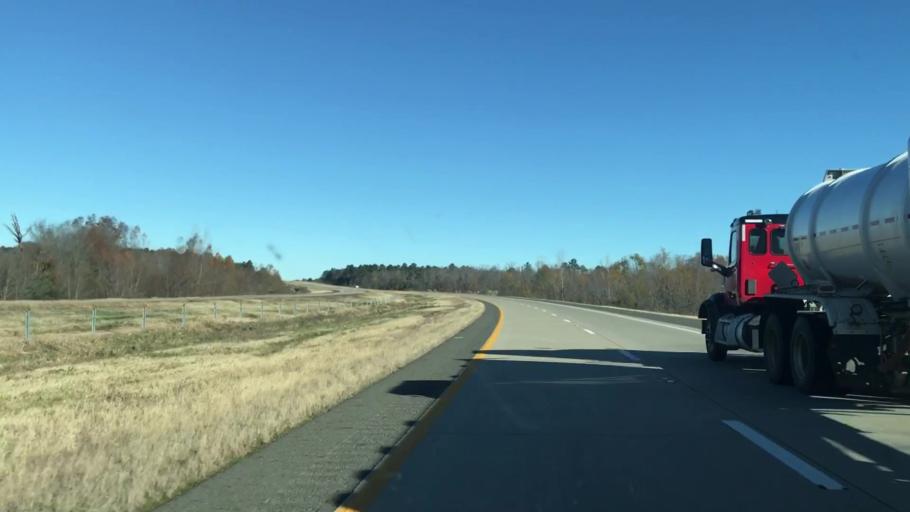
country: US
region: Texas
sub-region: Cass County
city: Queen City
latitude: 33.1687
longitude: -93.8784
